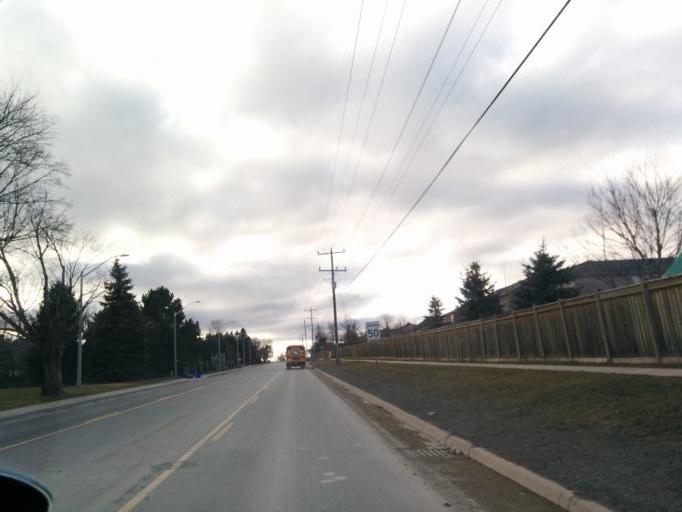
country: CA
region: Ontario
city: Bradford West Gwillimbury
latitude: 44.0978
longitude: -79.5802
